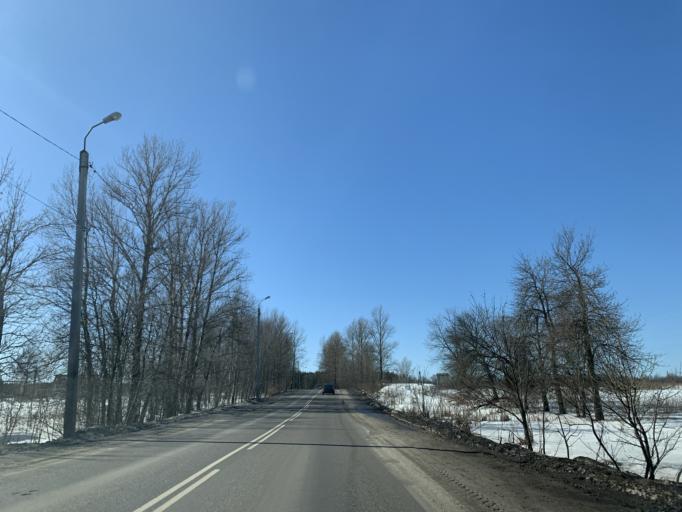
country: RU
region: Jaroslavl
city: Konstantinovskiy
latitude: 57.8363
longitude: 39.5622
